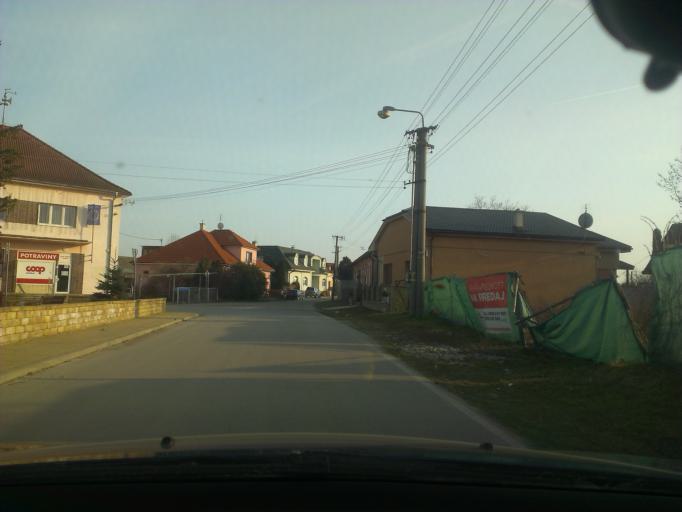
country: SK
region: Trnavsky
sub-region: Okres Trnava
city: Piestany
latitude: 48.6575
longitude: 17.8460
